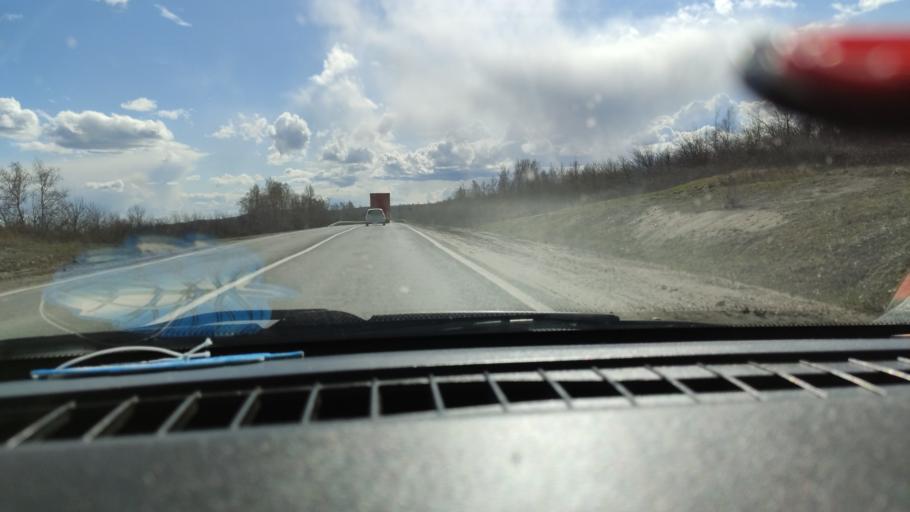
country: RU
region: Saratov
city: Dukhovnitskoye
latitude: 52.6759
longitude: 48.2271
